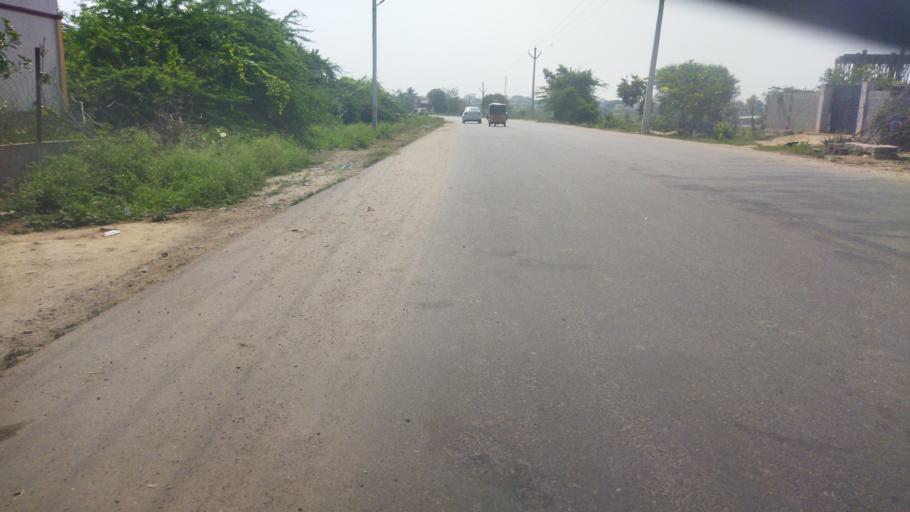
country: IN
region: Telangana
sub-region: Nalgonda
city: Nalgonda
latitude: 17.0788
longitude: 79.2835
